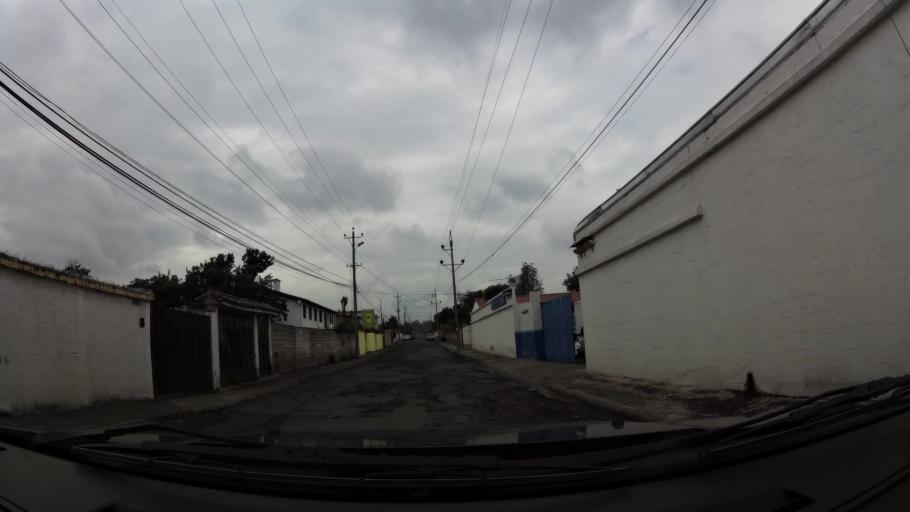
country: EC
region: Pichincha
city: Sangolqui
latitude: -0.3028
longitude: -78.4639
